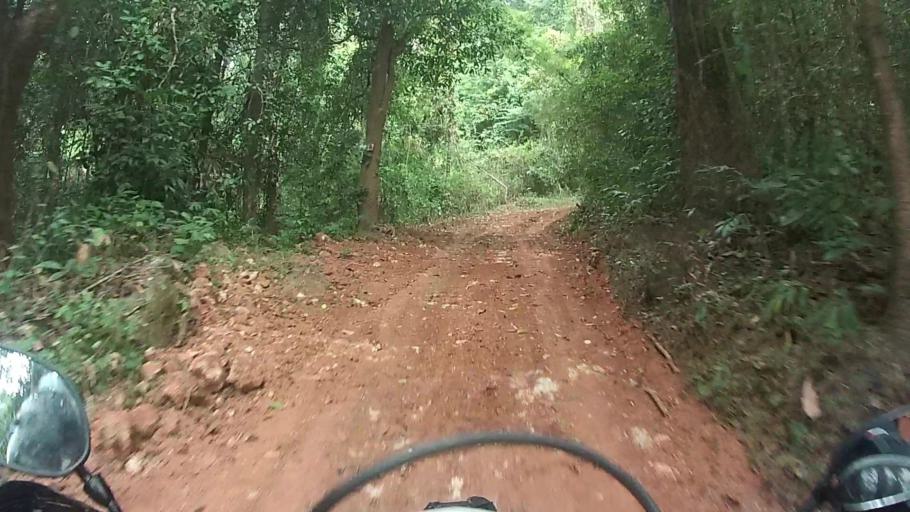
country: TH
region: Chiang Mai
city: Mae On
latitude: 18.7989
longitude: 99.3527
